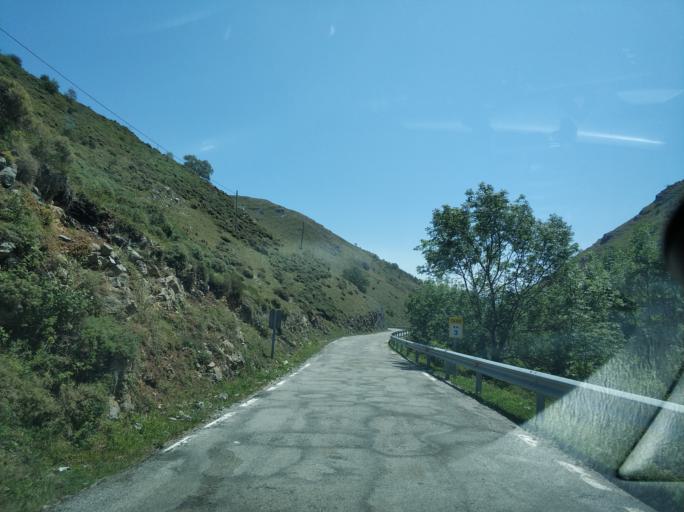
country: ES
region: Cantabria
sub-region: Provincia de Cantabria
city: Reinosa
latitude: 43.0312
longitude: -4.1709
